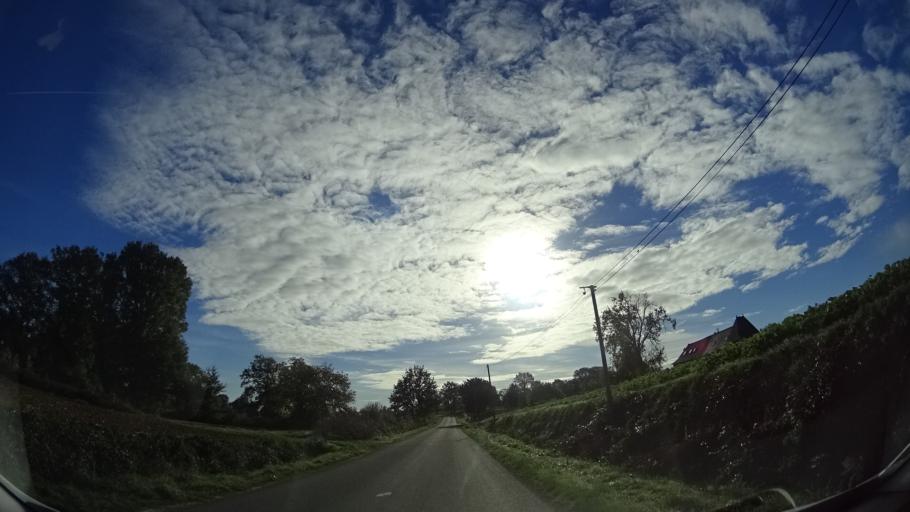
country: FR
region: Brittany
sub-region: Departement d'Ille-et-Vilaine
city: Geveze
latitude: 48.1910
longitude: -1.8126
